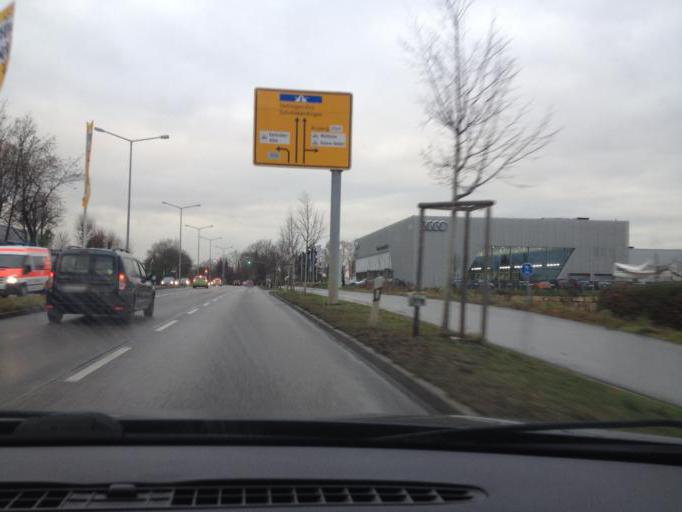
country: DE
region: Baden-Wuerttemberg
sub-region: Regierungsbezirk Stuttgart
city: Asperg
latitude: 48.8902
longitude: 9.1603
